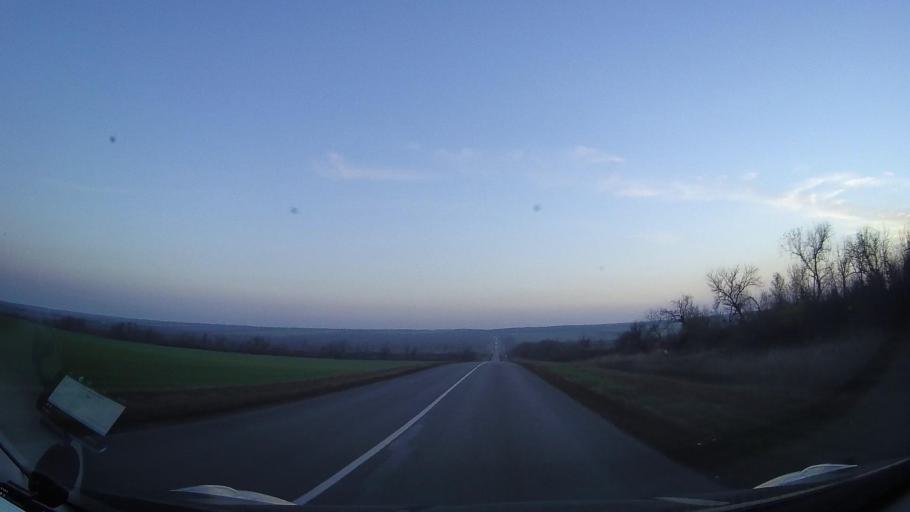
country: RU
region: Rostov
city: Zernograd
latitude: 46.9067
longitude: 40.3388
